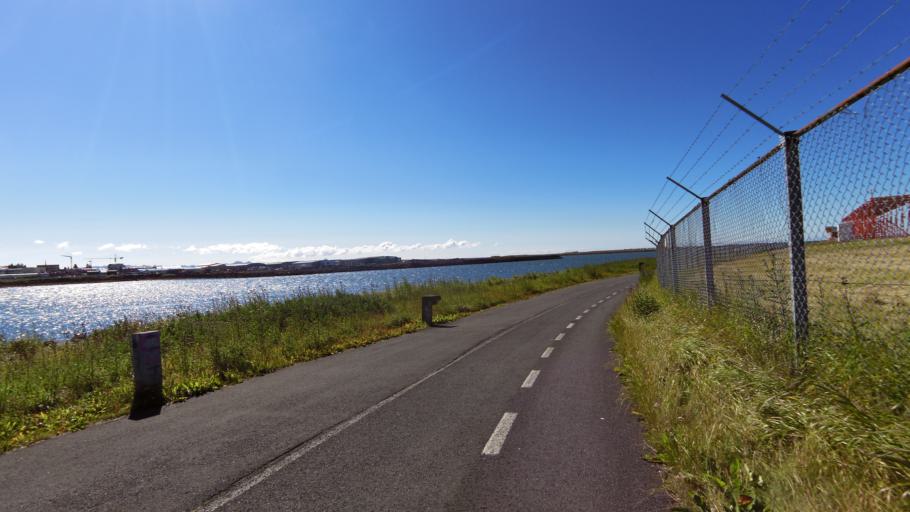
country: IS
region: Capital Region
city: Kopavogur
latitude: 64.1207
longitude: -21.9346
